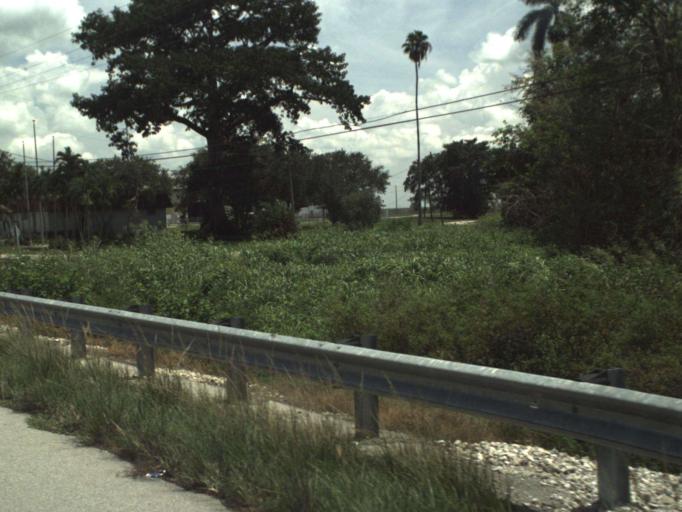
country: US
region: Florida
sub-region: Palm Beach County
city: Pahokee
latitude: 26.8503
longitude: -80.6131
